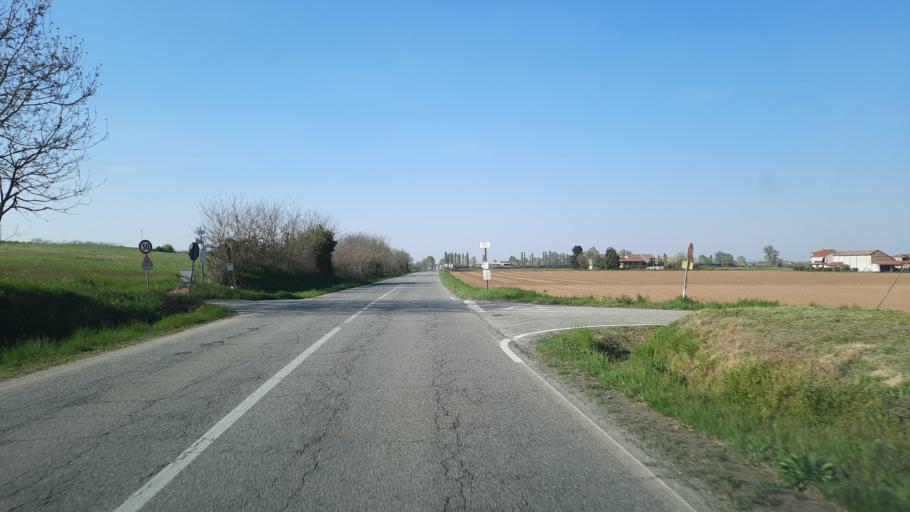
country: IT
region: Piedmont
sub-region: Provincia di Alessandria
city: Terruggia
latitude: 45.0677
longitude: 8.4678
